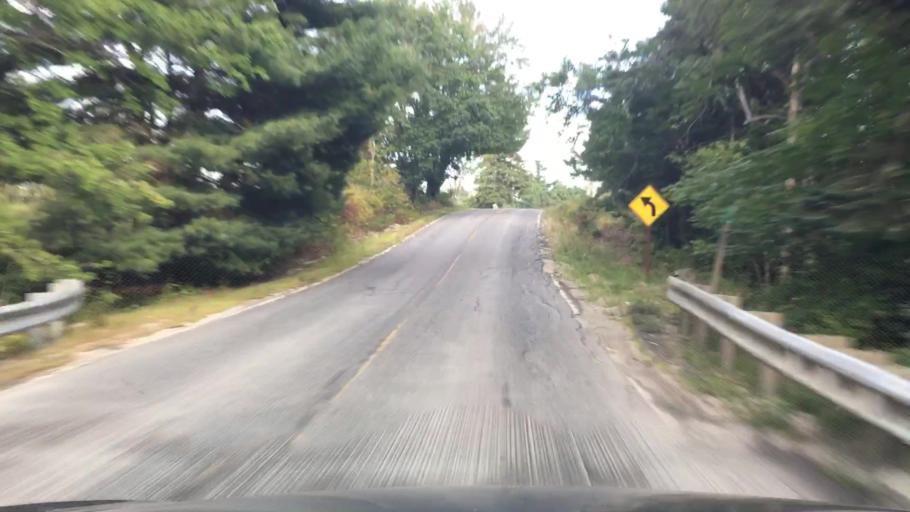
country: US
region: Maine
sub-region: Hancock County
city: Surry
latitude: 44.4943
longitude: -68.5198
